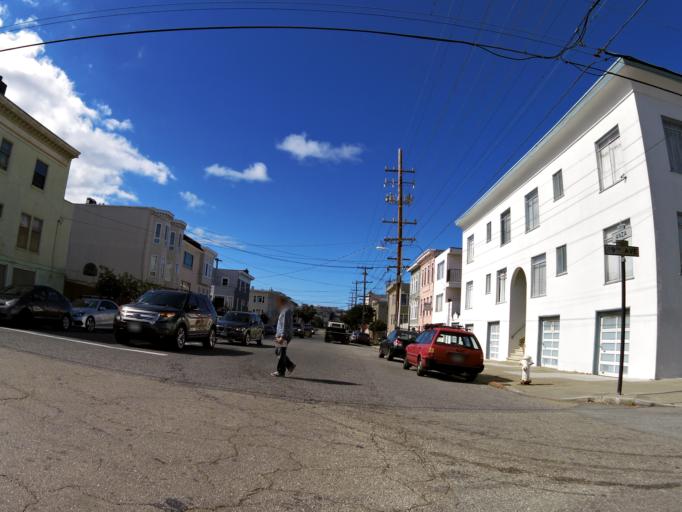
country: US
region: California
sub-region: San Francisco County
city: San Francisco
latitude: 37.7785
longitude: -122.4782
